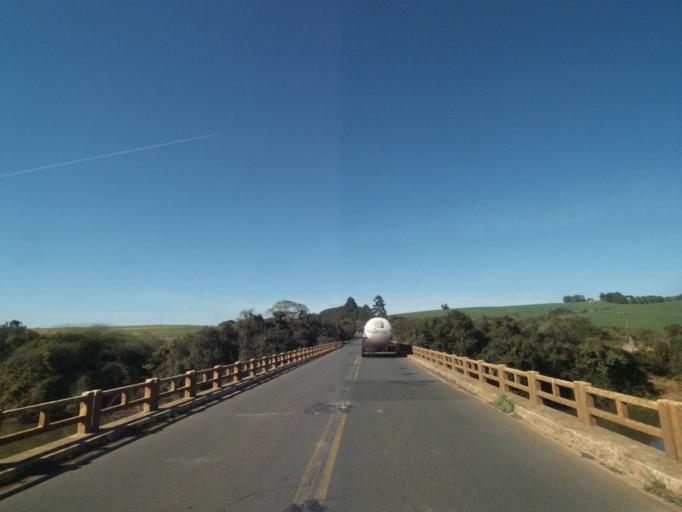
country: BR
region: Parana
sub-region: Tibagi
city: Tibagi
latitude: -24.4801
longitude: -50.4437
